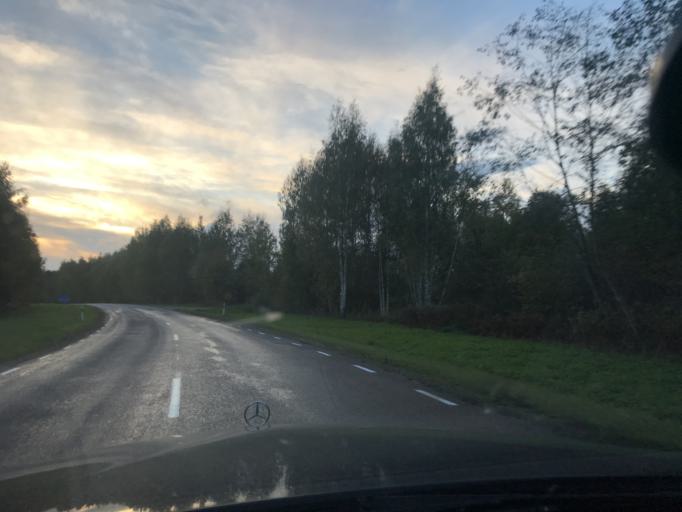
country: EE
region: Valgamaa
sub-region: Torva linn
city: Torva
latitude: 58.0125
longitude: 26.1732
